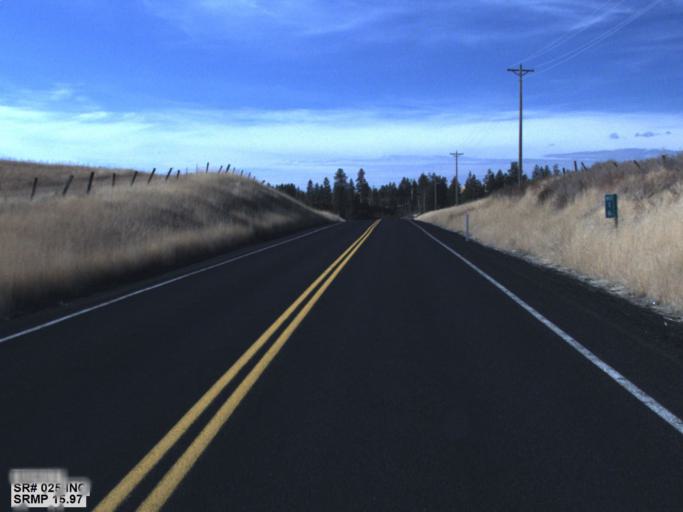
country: US
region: Washington
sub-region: Lincoln County
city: Davenport
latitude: 47.8613
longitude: -118.2237
